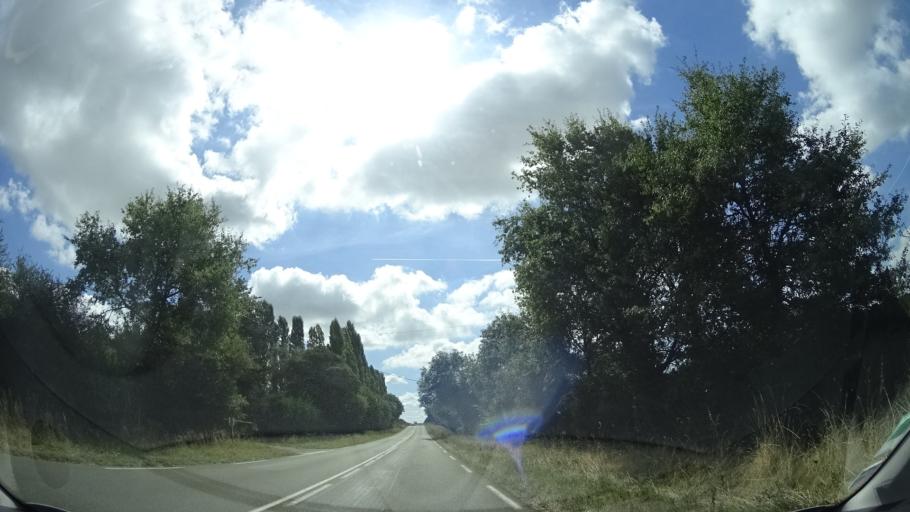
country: FR
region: Pays de la Loire
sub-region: Departement de la Mayenne
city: Meslay-du-Maine
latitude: 47.9410
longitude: -0.5164
